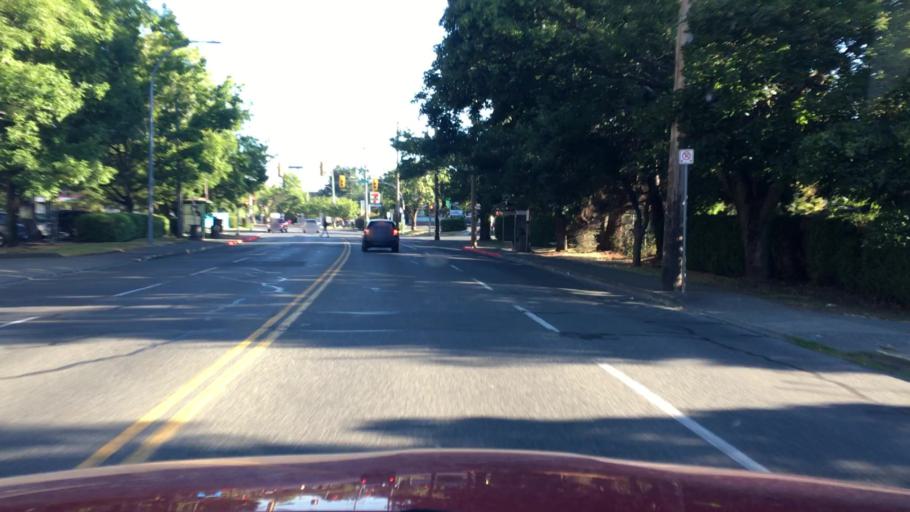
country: CA
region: British Columbia
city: Oak Bay
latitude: 48.4753
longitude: -123.3327
